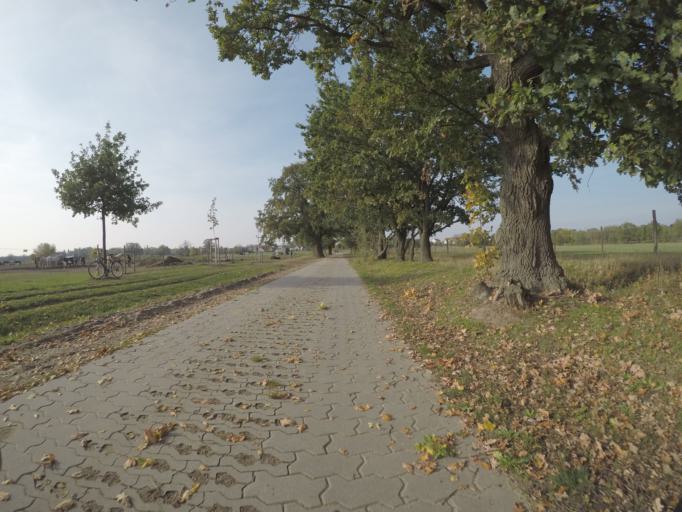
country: DE
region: Berlin
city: Gropiusstadt
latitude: 52.3984
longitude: 13.4615
